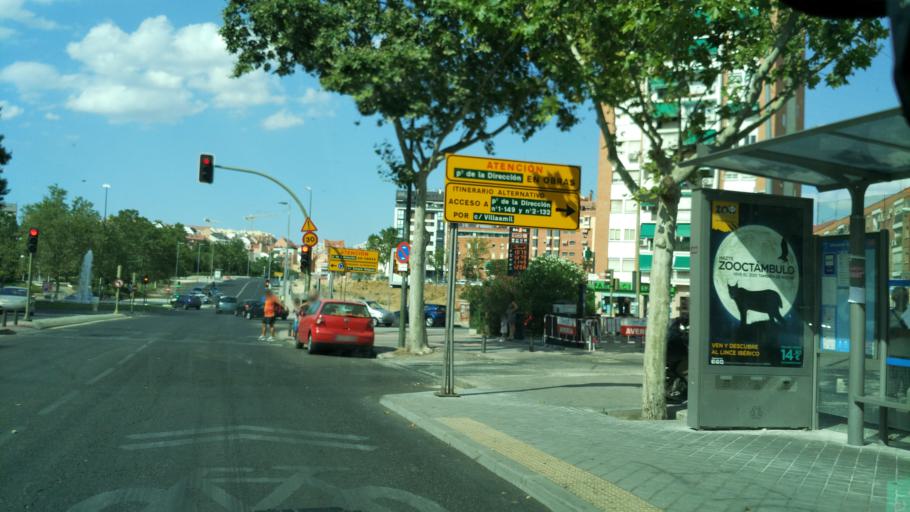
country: ES
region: Madrid
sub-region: Provincia de Madrid
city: Tetuan de las Victorias
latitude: 40.4615
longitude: -3.7088
